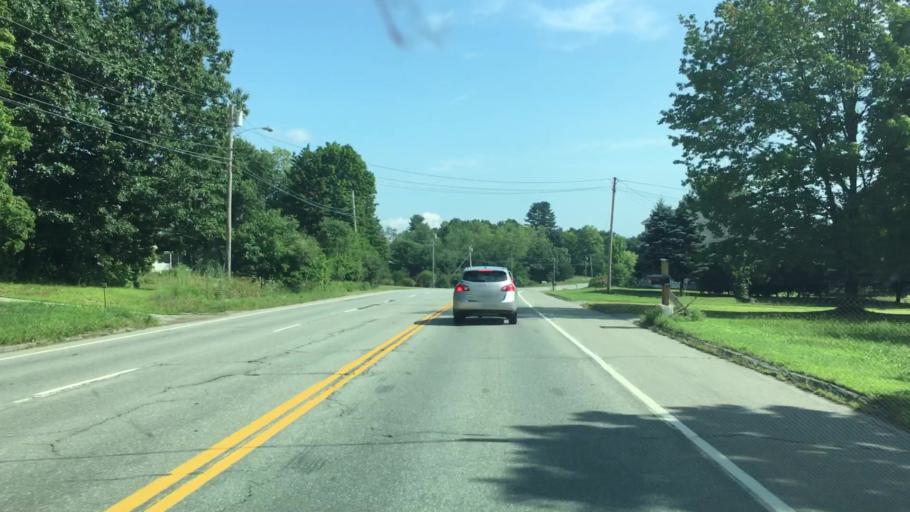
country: US
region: Maine
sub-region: Penobscot County
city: Orrington
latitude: 44.7054
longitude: -68.8457
